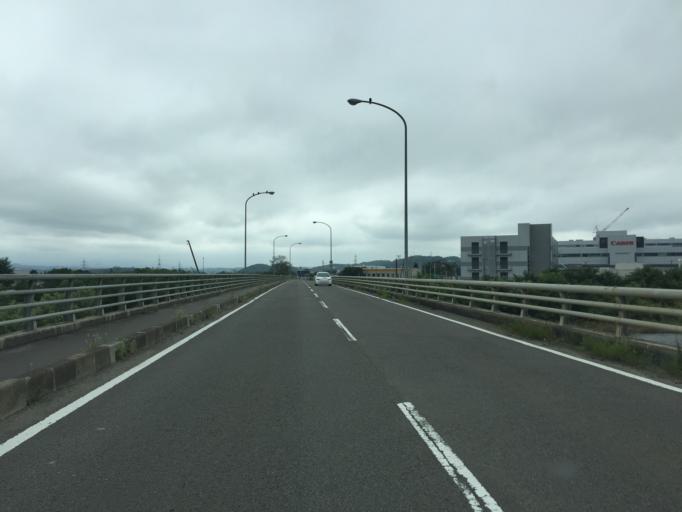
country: JP
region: Fukushima
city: Fukushima-shi
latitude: 37.7468
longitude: 140.4032
